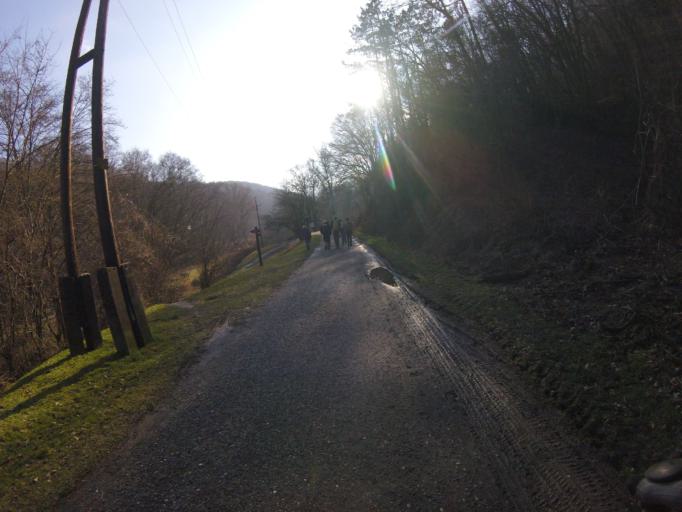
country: HU
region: Komarom-Esztergom
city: Pilismarot
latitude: 47.7524
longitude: 18.9035
